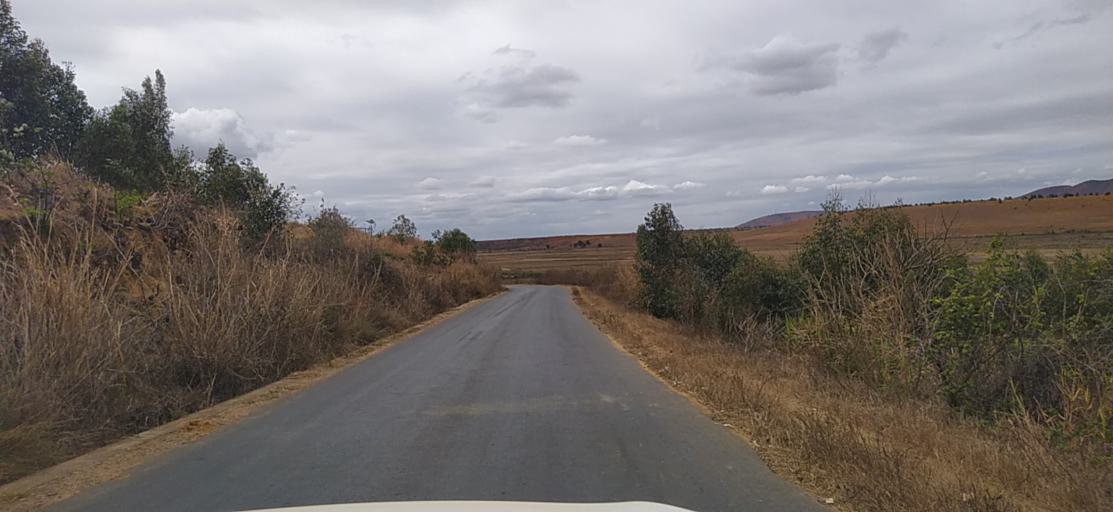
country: MG
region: Alaotra Mangoro
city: Ambatondrazaka
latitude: -17.9266
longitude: 48.2579
